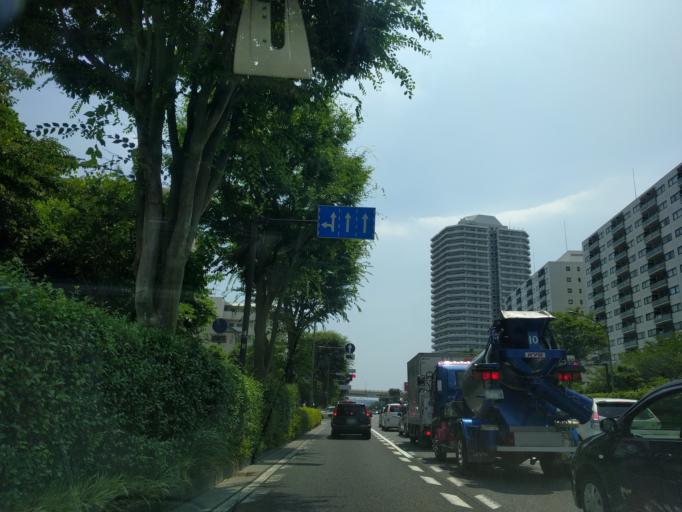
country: JP
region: Kanagawa
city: Yokohama
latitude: 35.4326
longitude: 139.5632
